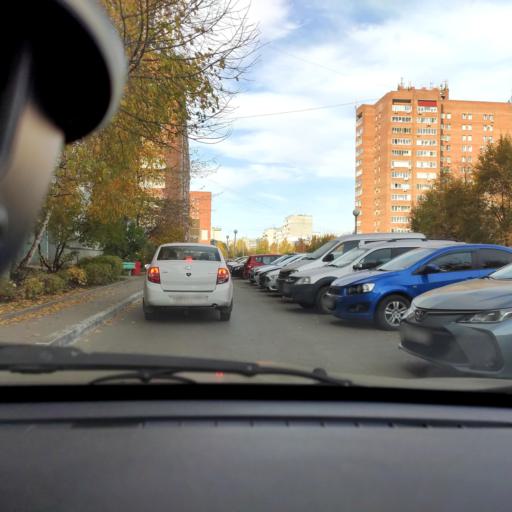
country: RU
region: Samara
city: Tol'yatti
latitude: 53.5440
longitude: 49.3499
